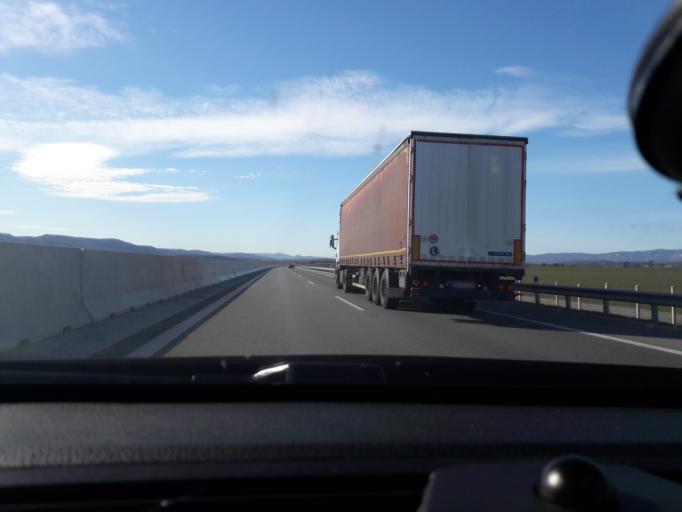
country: SK
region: Banskobystricky
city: Hrochot,Slovakia
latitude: 48.5702
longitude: 19.2892
